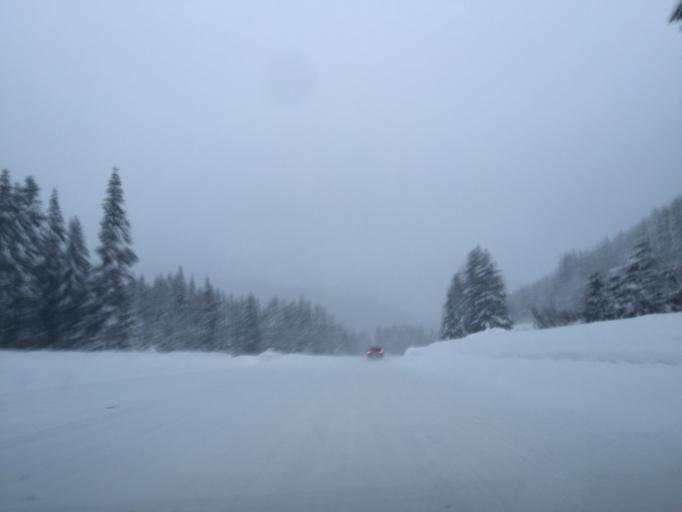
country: US
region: Washington
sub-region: Chelan County
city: Leavenworth
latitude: 47.7653
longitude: -121.0776
